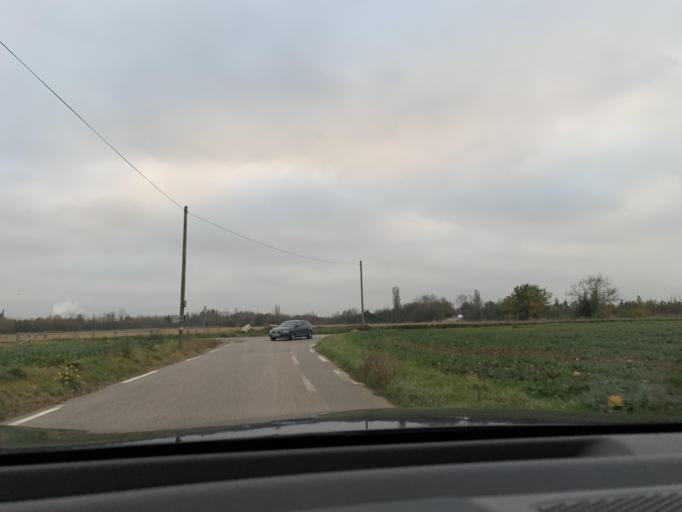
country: FR
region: Rhone-Alpes
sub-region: Departement du Rhone
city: Corbas
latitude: 45.6603
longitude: 4.9177
